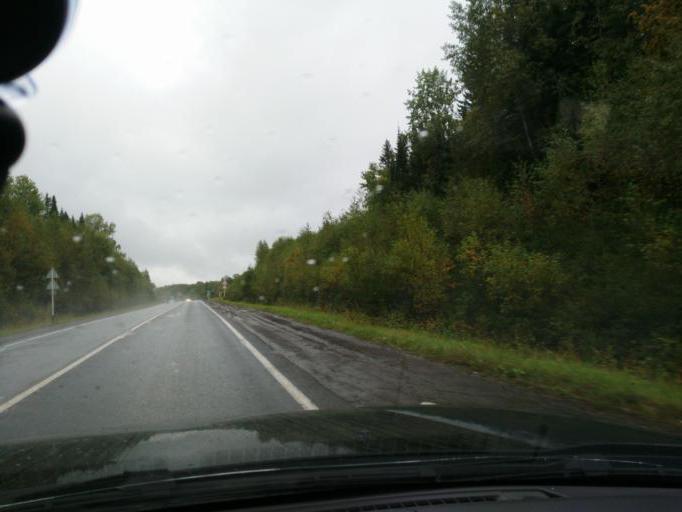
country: RU
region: Perm
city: Yugo-Kamskiy
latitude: 57.7298
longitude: 55.6990
